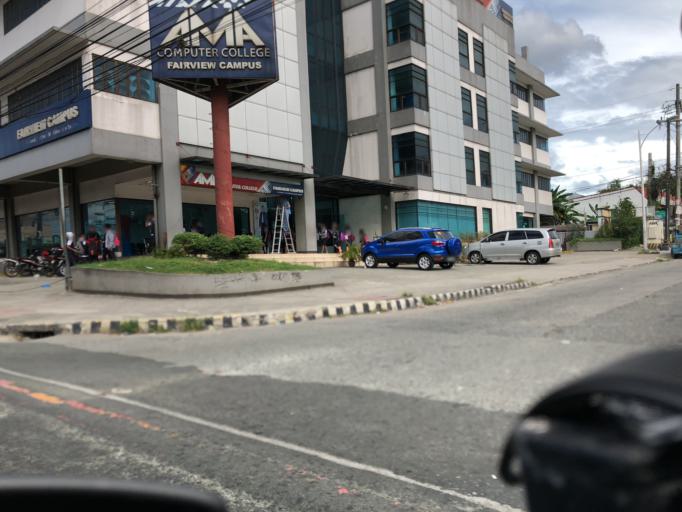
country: PH
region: Calabarzon
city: Bagong Pagasa
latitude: 14.7199
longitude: 121.0612
